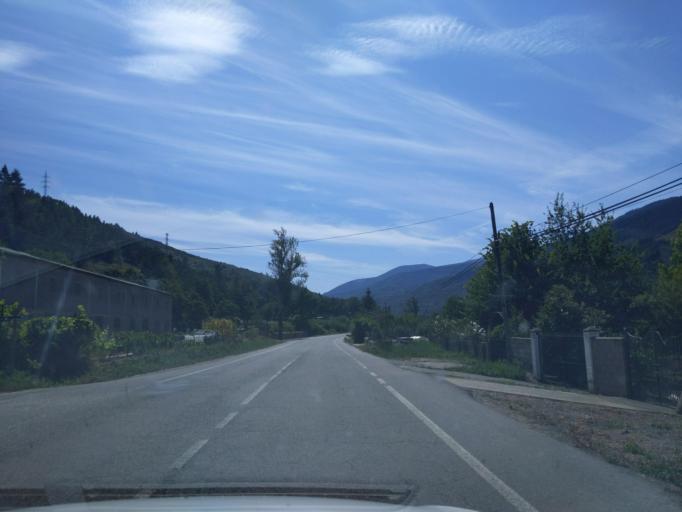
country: ES
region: La Rioja
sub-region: Provincia de La Rioja
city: Ezcaray
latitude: 42.3169
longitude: -3.0129
